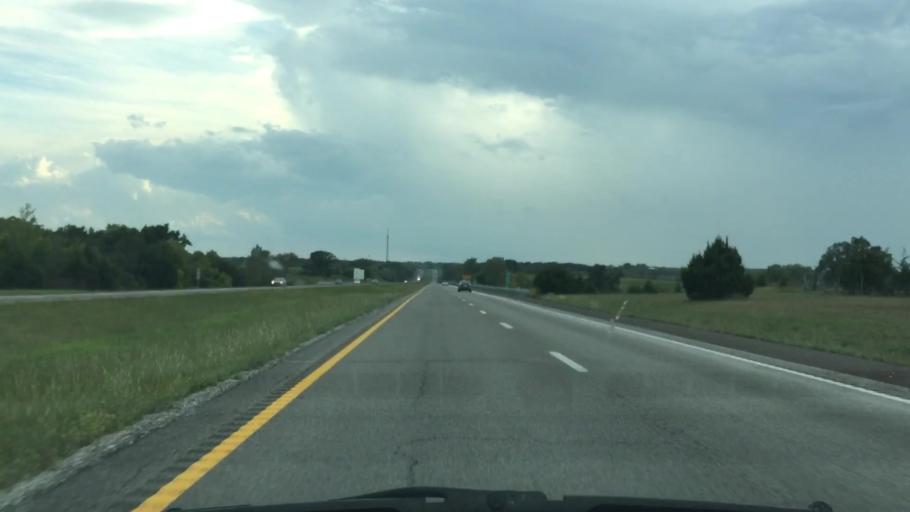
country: US
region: Missouri
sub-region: Clinton County
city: Cameron
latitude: 39.8880
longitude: -94.1580
